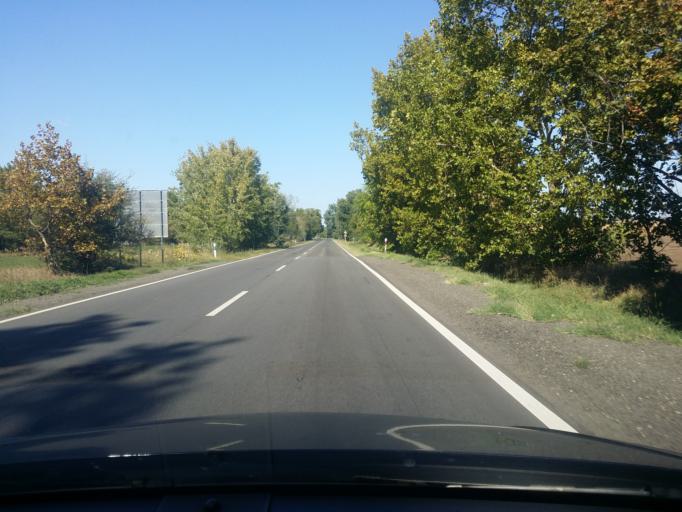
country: HU
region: Bacs-Kiskun
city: Kiskunfelegyhaza
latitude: 46.6518
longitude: 19.8742
